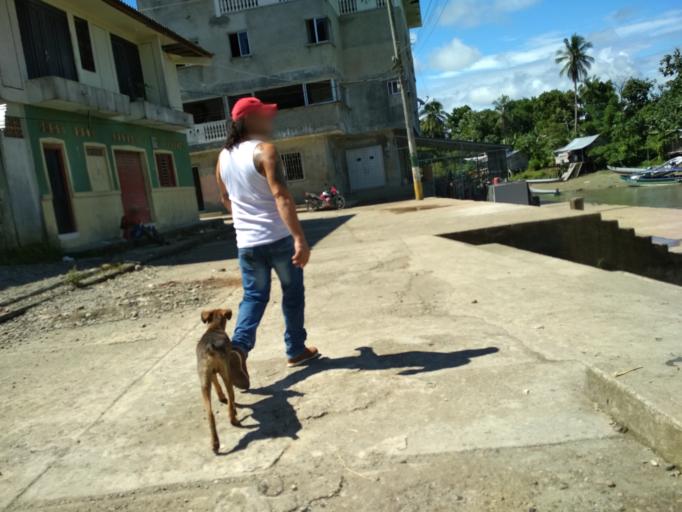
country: CO
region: Cauca
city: Timbiqui
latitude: 2.7707
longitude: -77.6643
